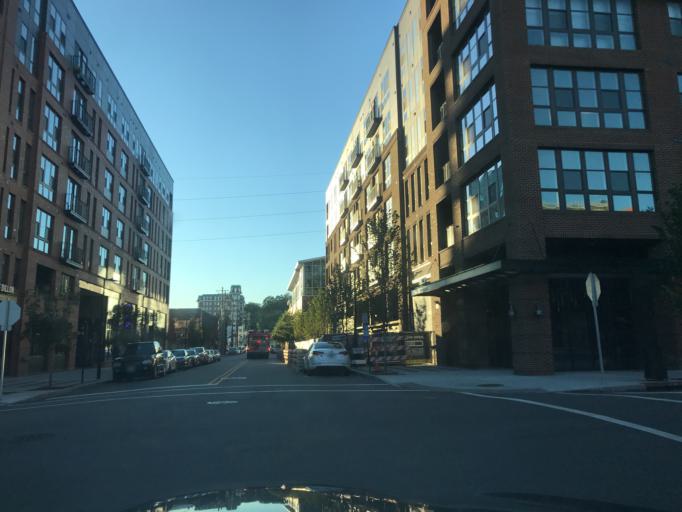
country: US
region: North Carolina
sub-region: Wake County
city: Raleigh
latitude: 35.7785
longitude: -78.6450
